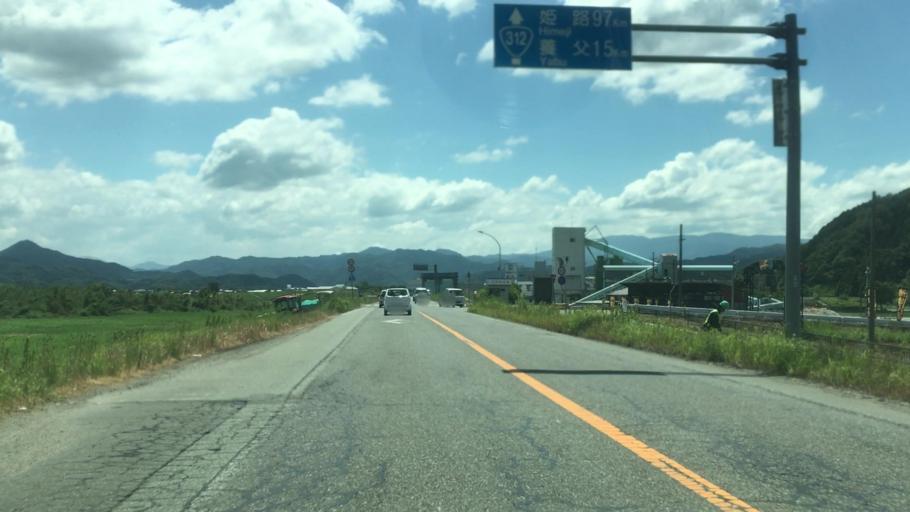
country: JP
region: Hyogo
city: Toyooka
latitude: 35.5058
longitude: 134.8137
